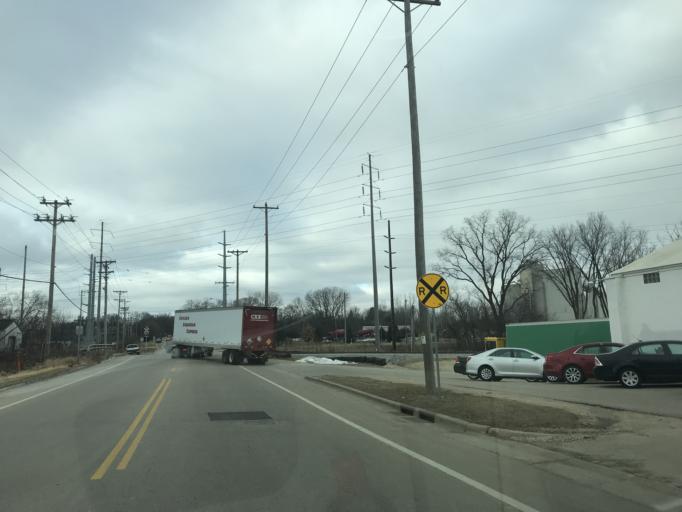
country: US
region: Wisconsin
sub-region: Dane County
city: Monona
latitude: 43.1137
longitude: -89.3095
